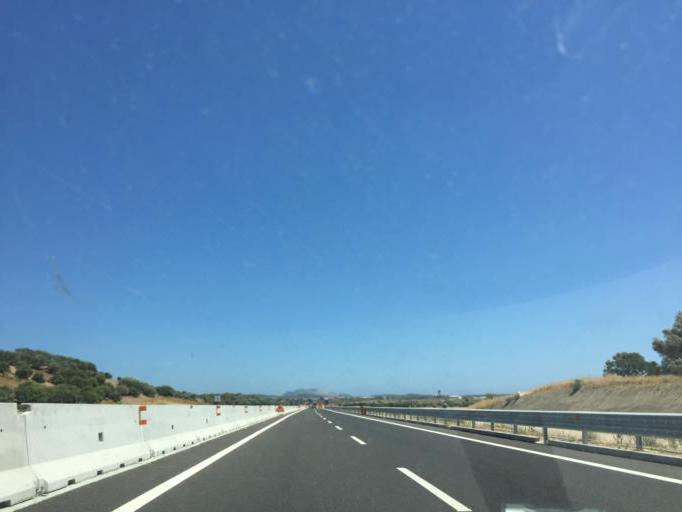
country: IT
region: Sardinia
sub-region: Provincia di Olbia-Tempio
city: Olbia
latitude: 40.8865
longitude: 9.4760
